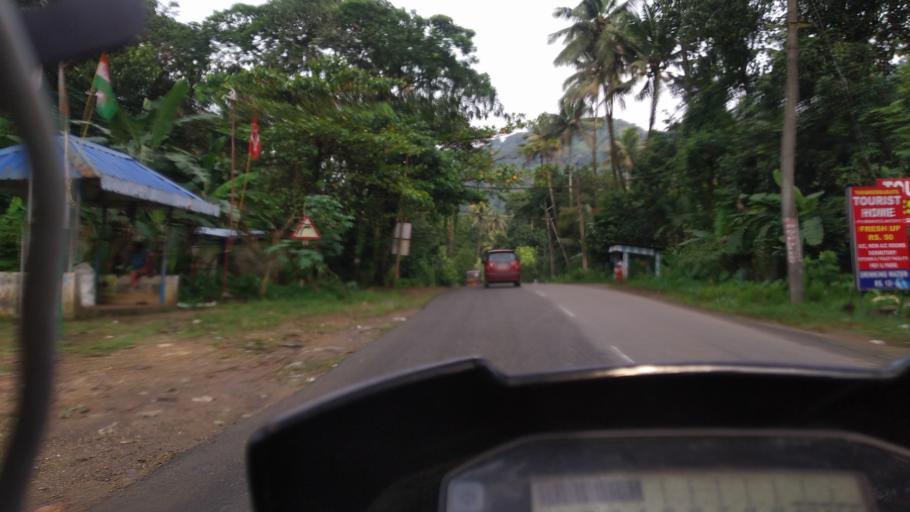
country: IN
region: Kerala
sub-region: Idukki
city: Kuttampuzha
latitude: 10.0507
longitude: 76.7554
